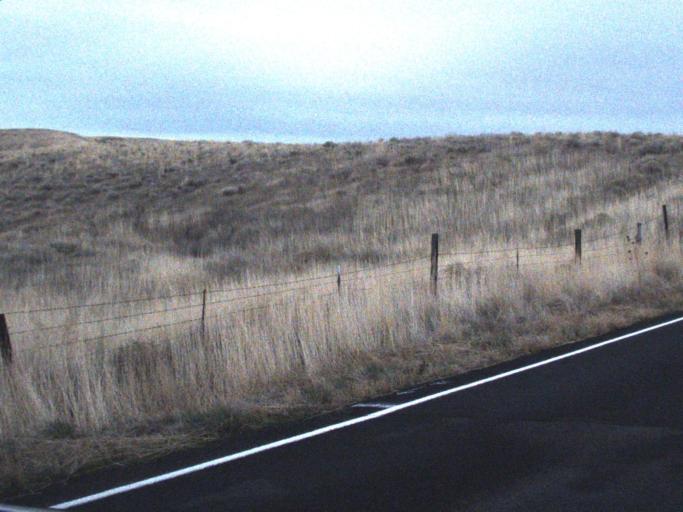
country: US
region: Washington
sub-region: Columbia County
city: Dayton
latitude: 46.5034
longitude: -118.0334
